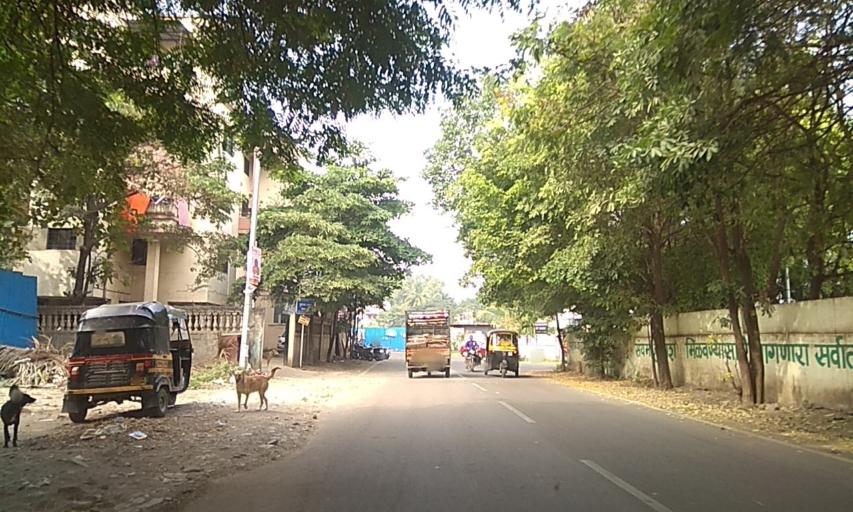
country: IN
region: Maharashtra
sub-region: Pune Division
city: Pune
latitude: 18.5044
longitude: 73.9304
